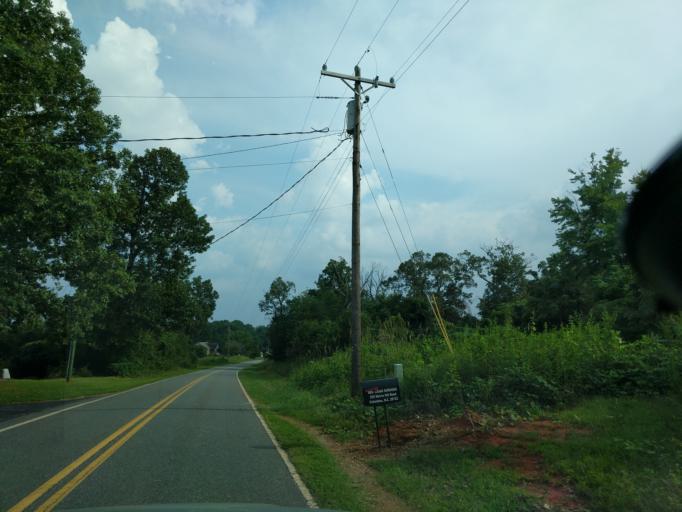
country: US
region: South Carolina
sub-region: Spartanburg County
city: Boiling Springs
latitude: 35.2036
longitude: -82.0218
